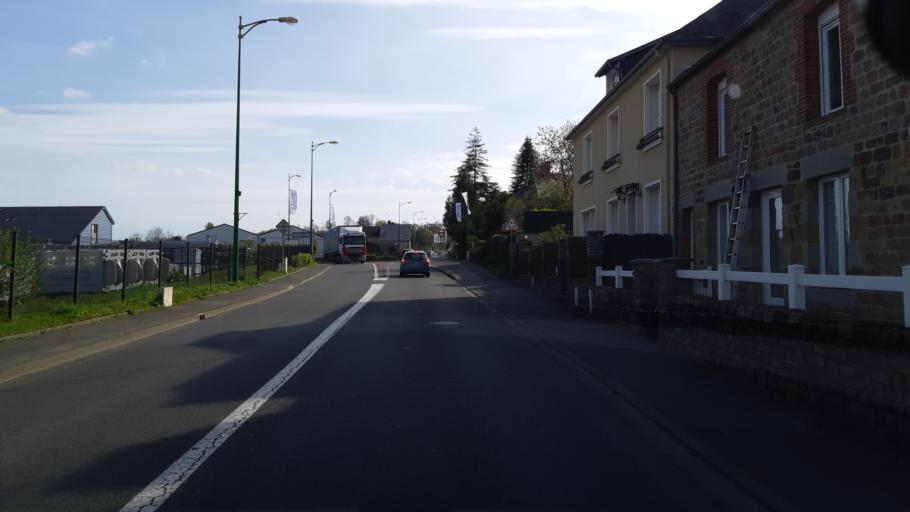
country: FR
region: Lower Normandy
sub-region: Departement de la Manche
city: Percy
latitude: 48.9120
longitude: -1.1949
